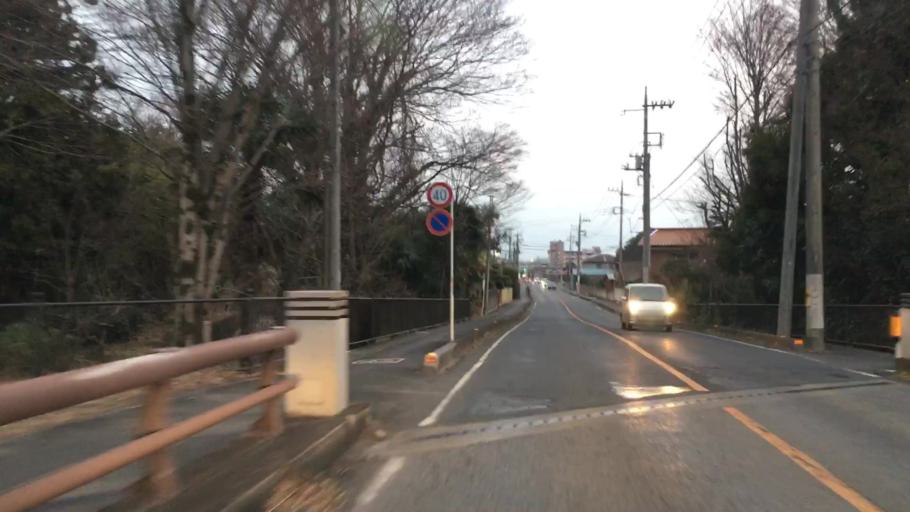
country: JP
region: Gunma
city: Ota
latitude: 36.3071
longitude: 139.3613
